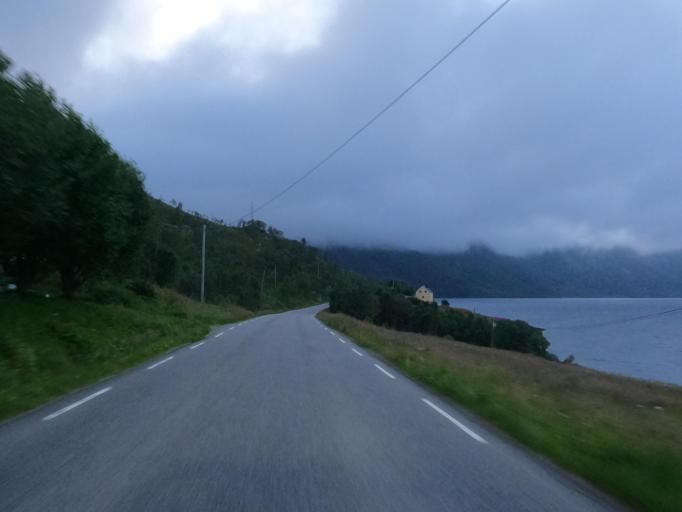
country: NO
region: Nordland
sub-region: Lodingen
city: Lodingen
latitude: 68.6070
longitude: 15.7782
